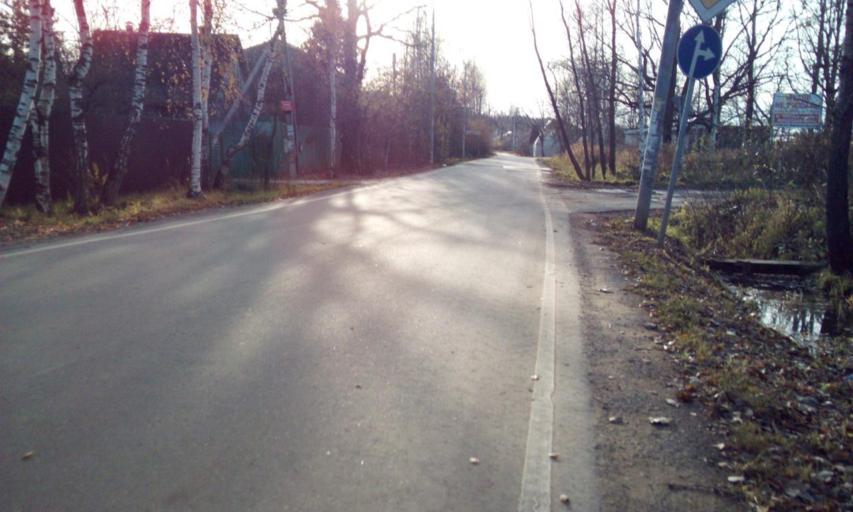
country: RU
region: Moskovskaya
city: Aprelevka
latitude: 55.5787
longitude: 37.1147
